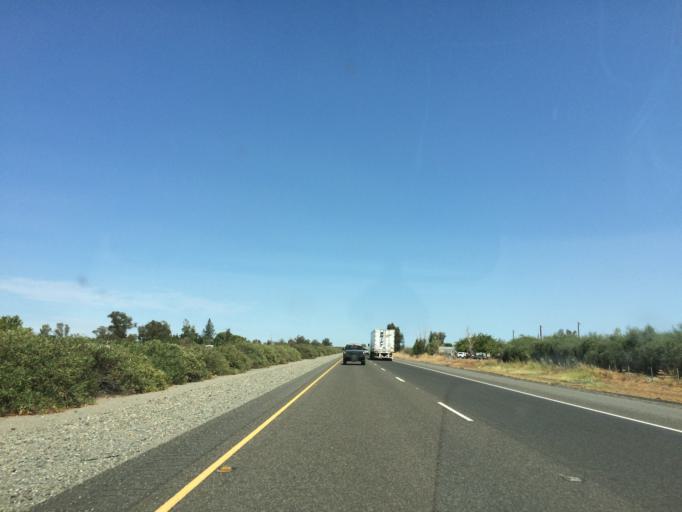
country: US
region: California
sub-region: Glenn County
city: Orland
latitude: 39.7173
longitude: -122.2059
